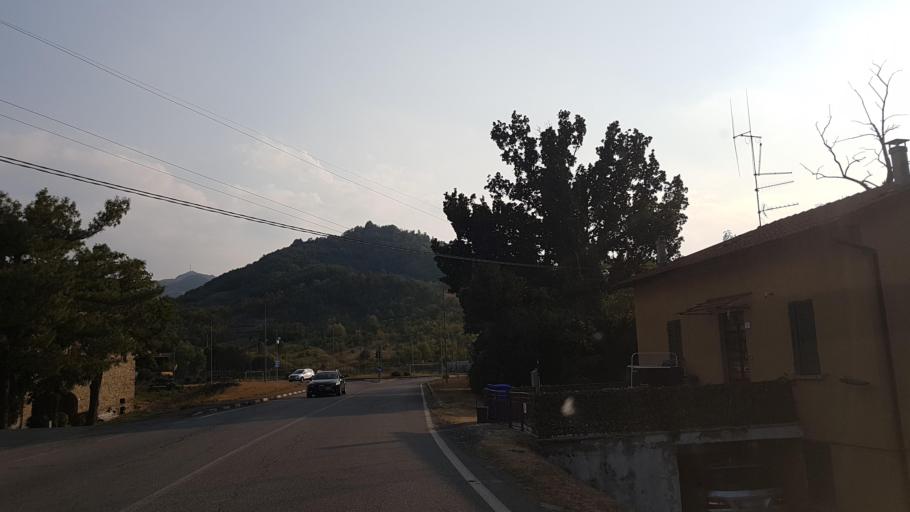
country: IT
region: Emilia-Romagna
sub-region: Provincia di Parma
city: Fornovo di Taro
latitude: 44.6799
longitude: 10.0948
